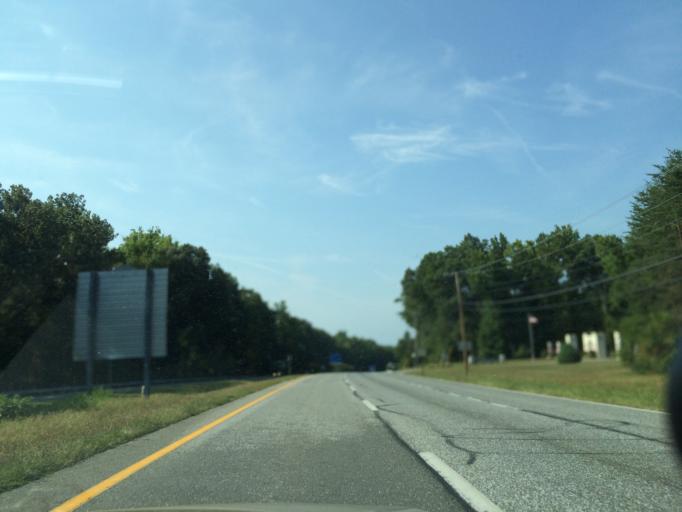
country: US
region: Virginia
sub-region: King George County
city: Dahlgren
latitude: 38.3725
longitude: -76.9592
